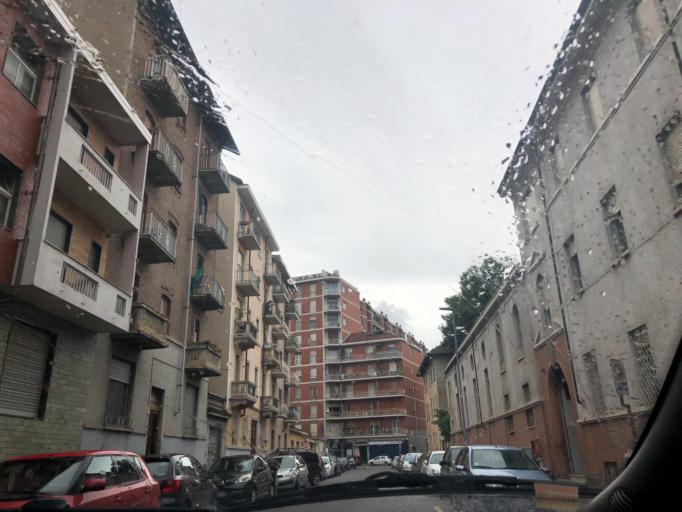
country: IT
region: Piedmont
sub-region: Provincia di Torino
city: Lesna
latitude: 45.0784
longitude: 7.6468
